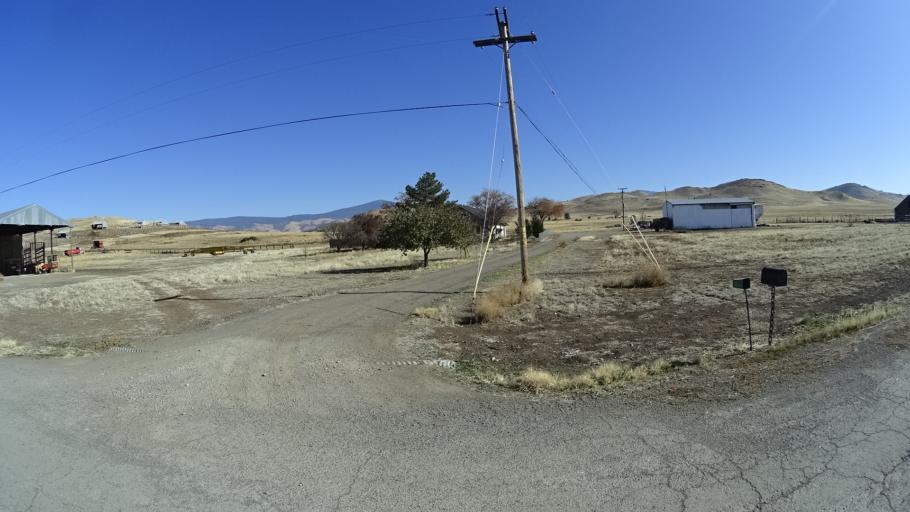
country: US
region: California
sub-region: Siskiyou County
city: Montague
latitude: 41.7884
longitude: -122.4345
